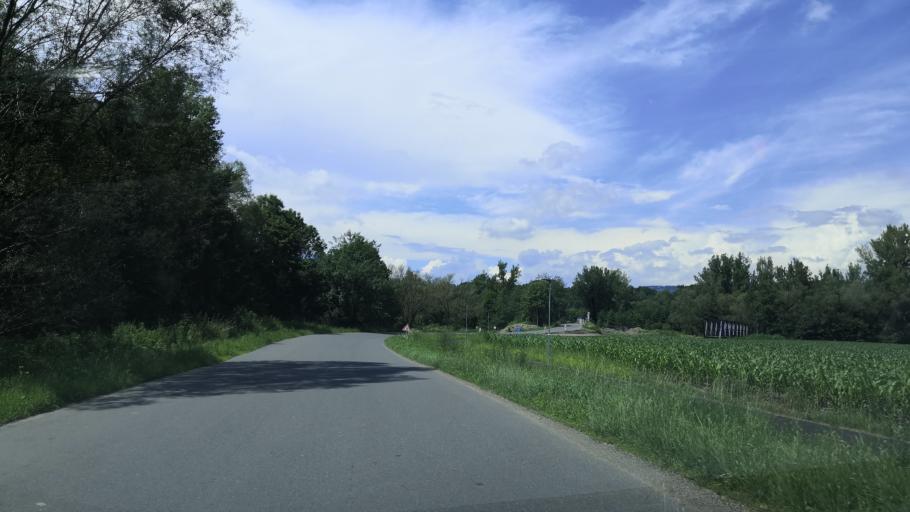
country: CZ
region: Zlin
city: Zasova
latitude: 49.4627
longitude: 18.0578
